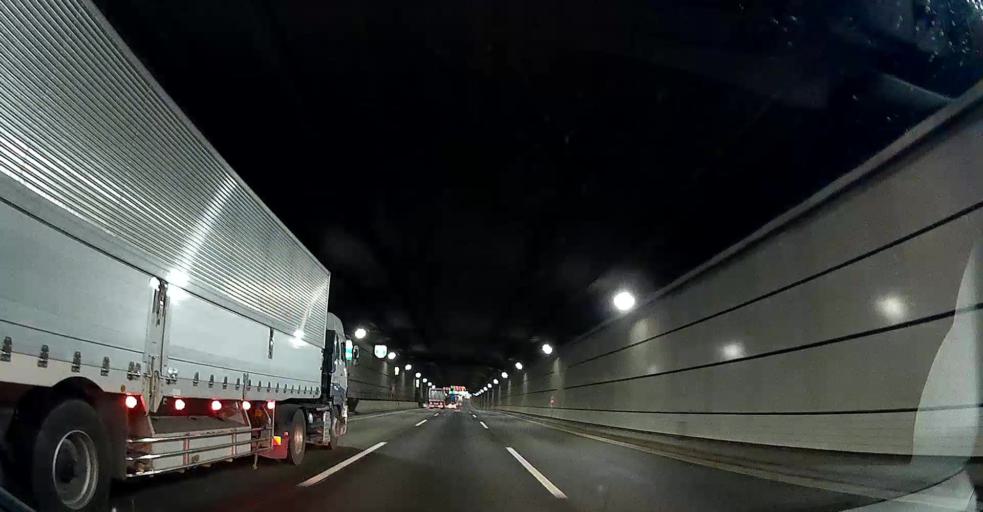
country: JP
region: Kanagawa
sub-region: Kawasaki-shi
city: Kawasaki
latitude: 35.5240
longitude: 139.7924
